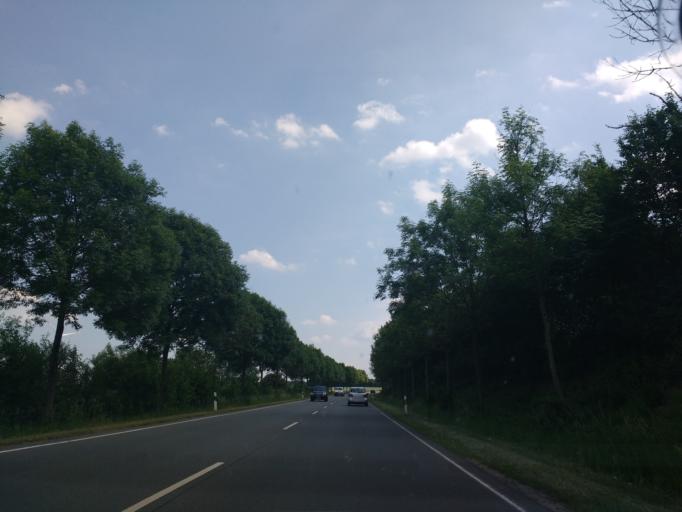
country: DE
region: North Rhine-Westphalia
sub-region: Regierungsbezirk Detmold
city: Paderborn
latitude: 51.7240
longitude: 8.8057
